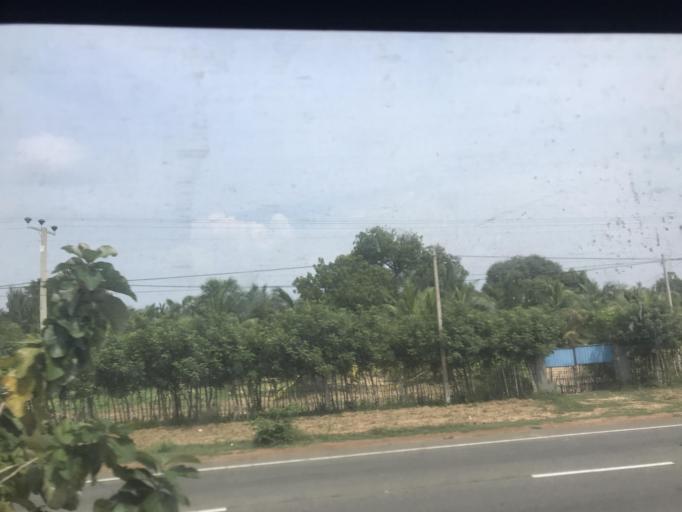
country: LK
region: Northern Province
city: Point Pedro
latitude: 9.6241
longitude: 80.3107
